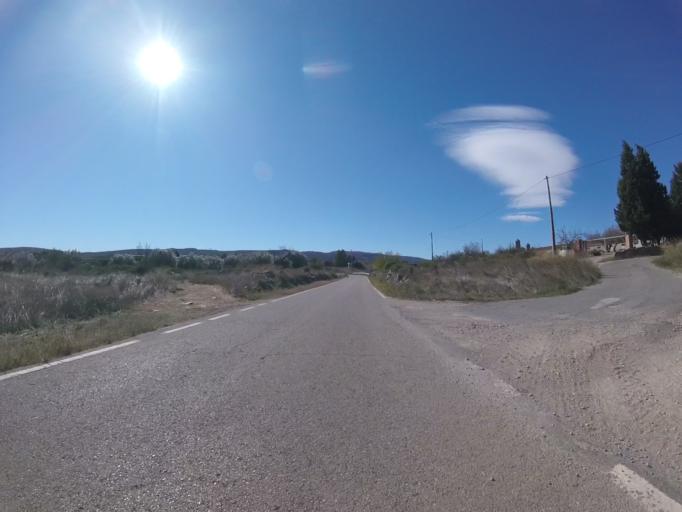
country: ES
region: Valencia
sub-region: Provincia de Castello
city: Albocasser
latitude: 40.3715
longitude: 0.0194
